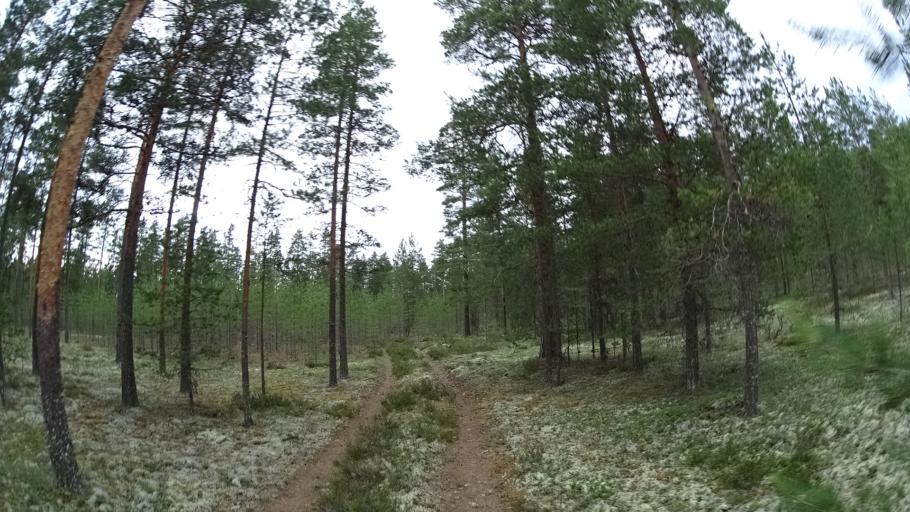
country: FI
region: Satakunta
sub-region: Pohjois-Satakunta
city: Jaemijaervi
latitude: 61.7643
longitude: 22.7609
